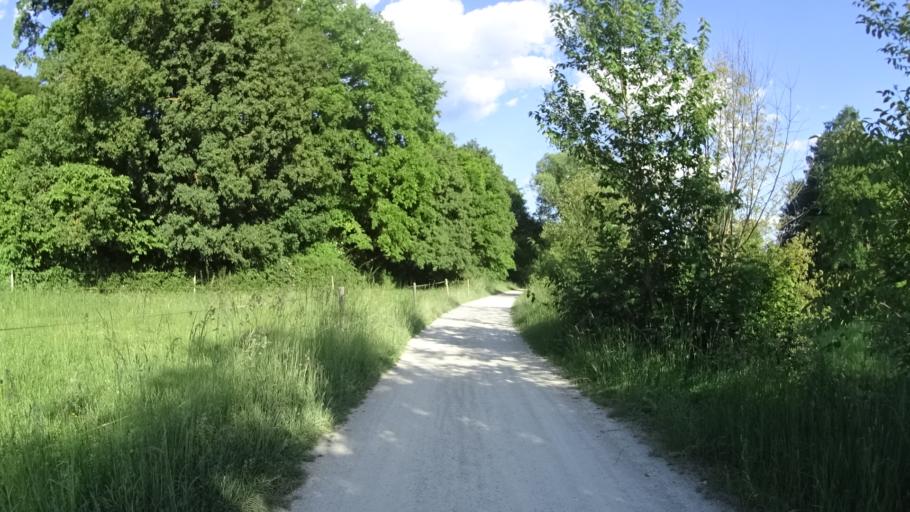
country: DE
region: Bavaria
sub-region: Upper Palatinate
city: Dietfurt
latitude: 49.0116
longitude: 11.6168
